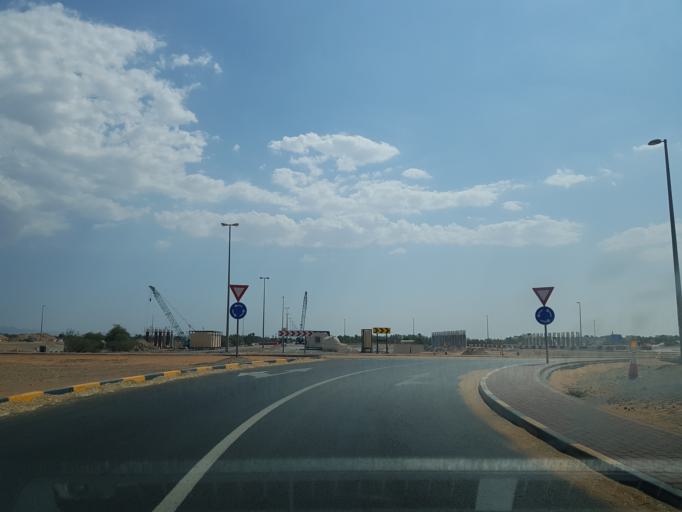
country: AE
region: Ash Shariqah
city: Adh Dhayd
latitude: 25.2334
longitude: 55.9168
